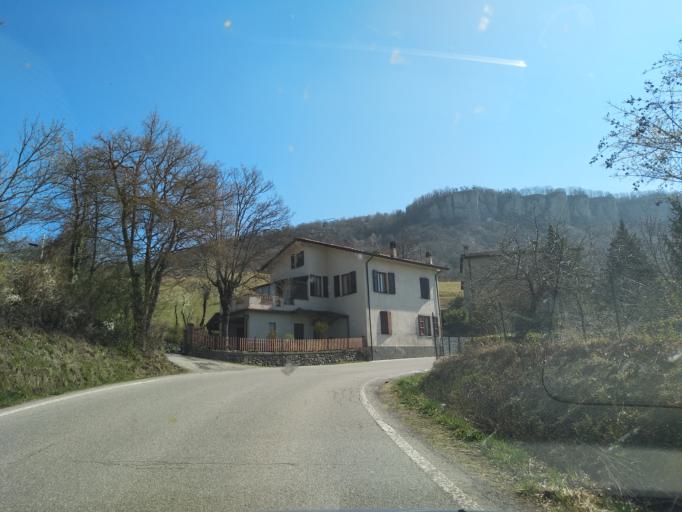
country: IT
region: Emilia-Romagna
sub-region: Provincia di Reggio Emilia
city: Castelnovo ne'Monti
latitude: 44.4292
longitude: 10.4092
